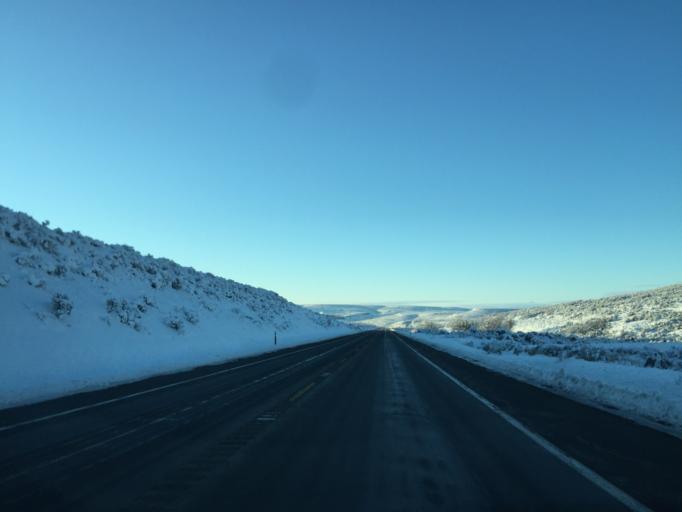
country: US
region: Washington
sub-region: Grant County
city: Soap Lake
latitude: 47.6018
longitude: -119.6201
